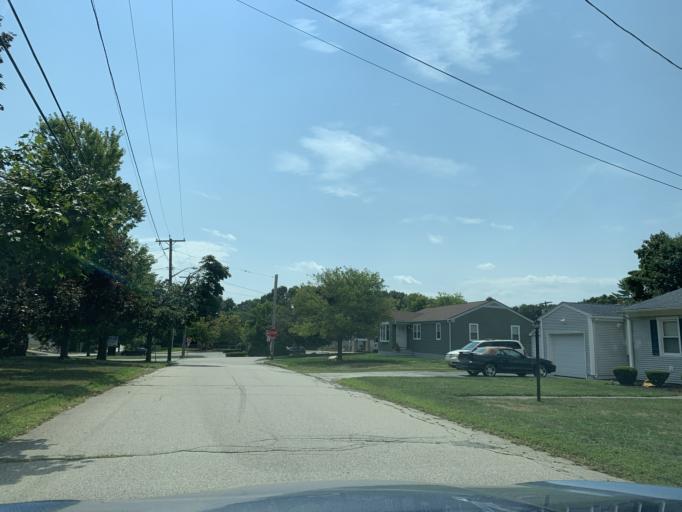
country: US
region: Rhode Island
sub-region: Providence County
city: Johnston
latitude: 41.7883
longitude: -71.4841
